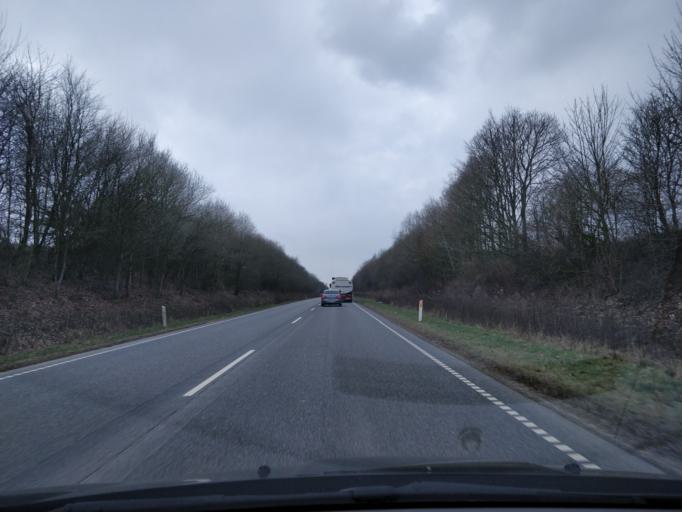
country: DK
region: South Denmark
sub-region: Vejle Kommune
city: Borkop
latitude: 55.6581
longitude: 9.6261
